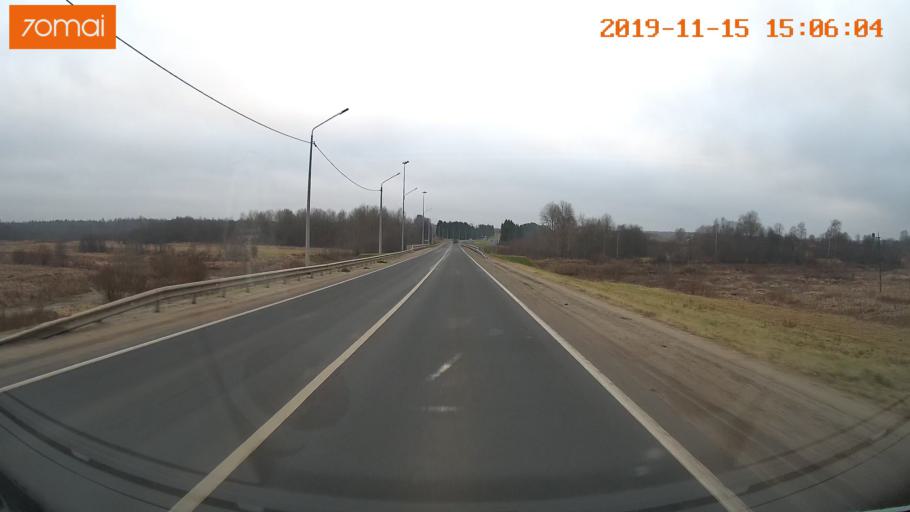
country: RU
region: Jaroslavl
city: Prechistoye
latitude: 58.3968
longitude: 40.3156
